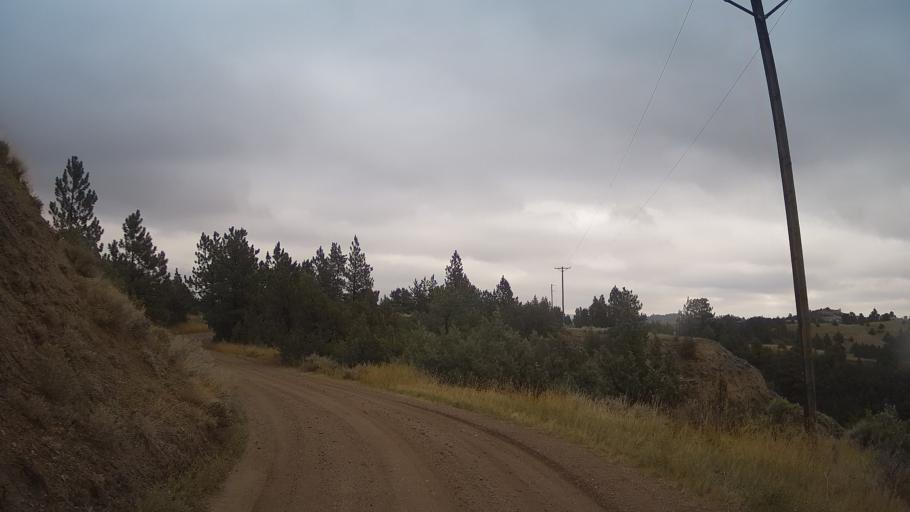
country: US
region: Montana
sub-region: Dawson County
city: Glendive
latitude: 47.0428
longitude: -104.6745
